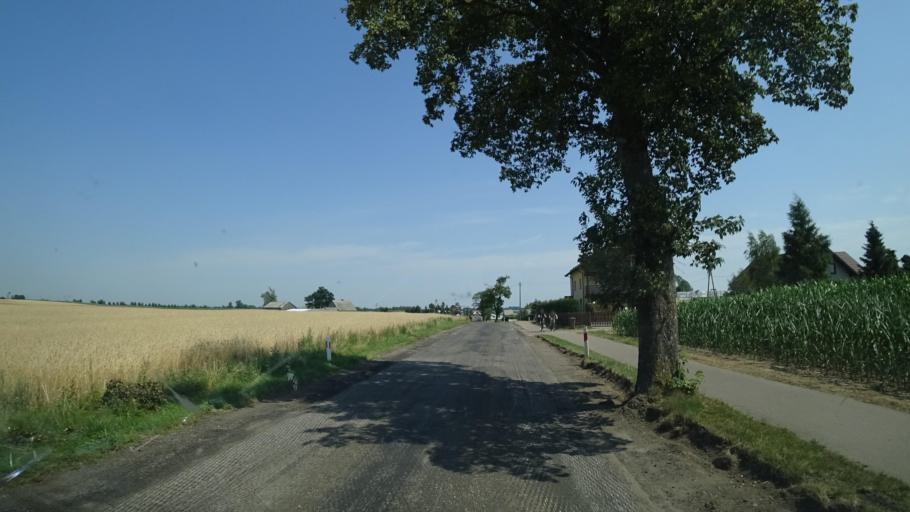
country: PL
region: Pomeranian Voivodeship
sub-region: Powiat chojnicki
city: Brusy
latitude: 53.8766
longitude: 17.6883
